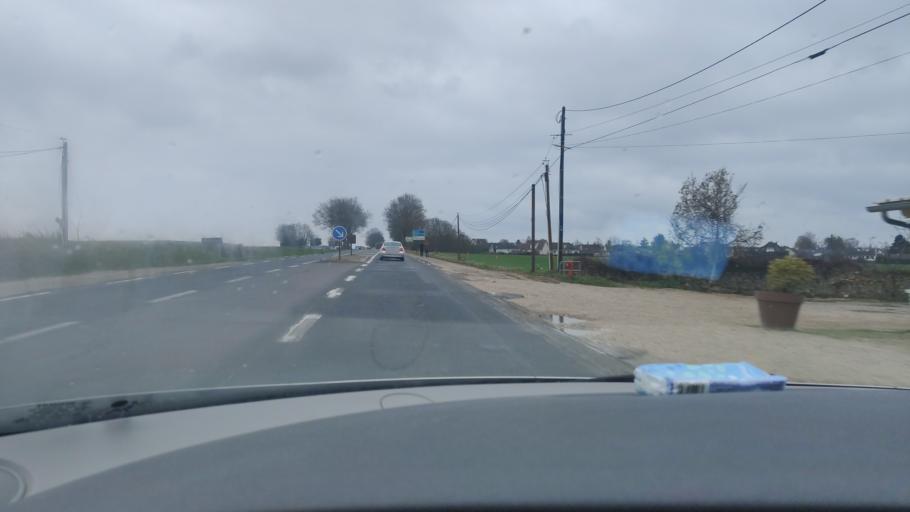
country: FR
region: Ile-de-France
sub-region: Departement de Seine-et-Marne
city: Vert-Saint-Denis
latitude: 48.5756
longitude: 2.6175
